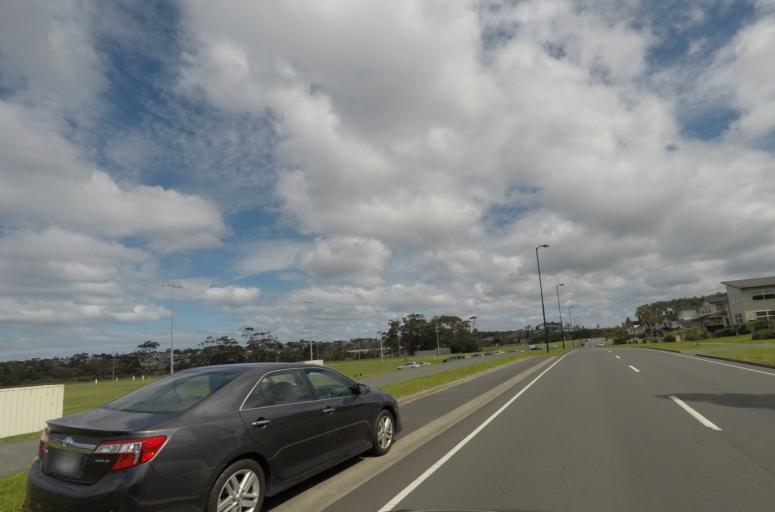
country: NZ
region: Auckland
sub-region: Auckland
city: Rothesay Bay
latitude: -36.6003
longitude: 174.6788
